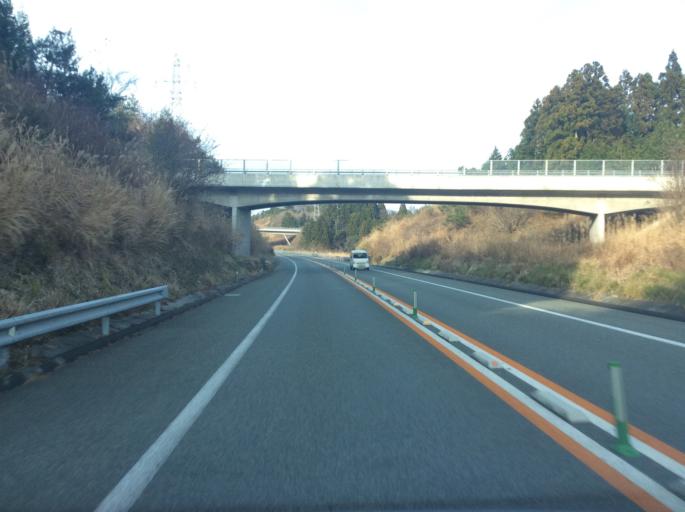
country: JP
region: Fukushima
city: Namie
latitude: 37.3381
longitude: 140.9907
